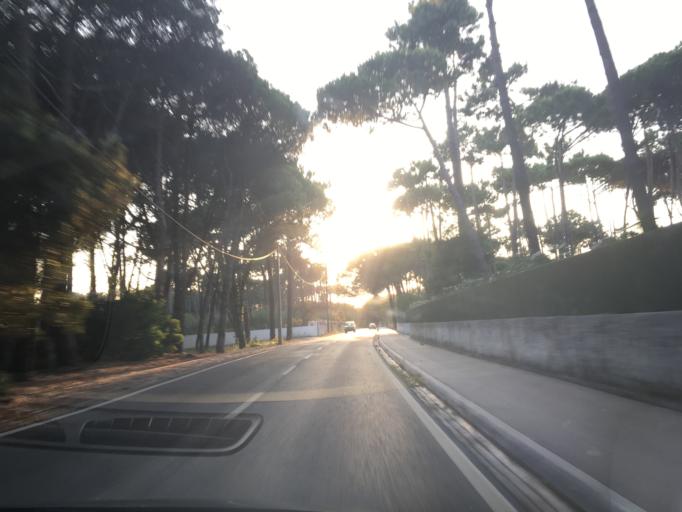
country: PT
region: Lisbon
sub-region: Sintra
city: Colares
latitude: 38.8310
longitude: -9.4471
